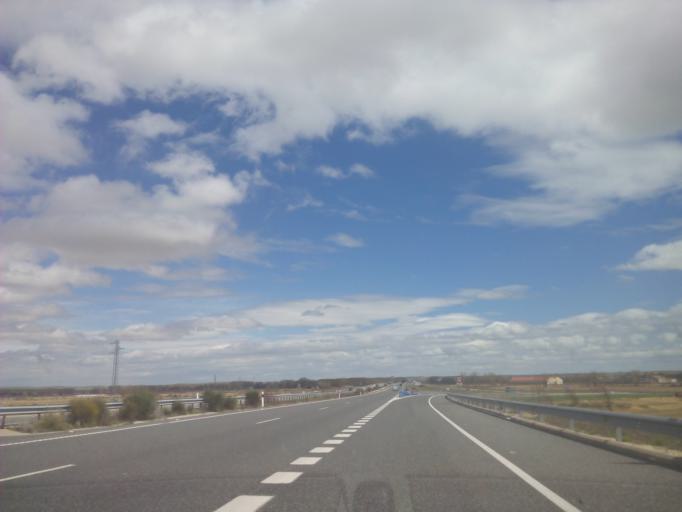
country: ES
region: Castille and Leon
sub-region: Provincia de Salamanca
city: Machacon
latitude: 40.9205
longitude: -5.5120
